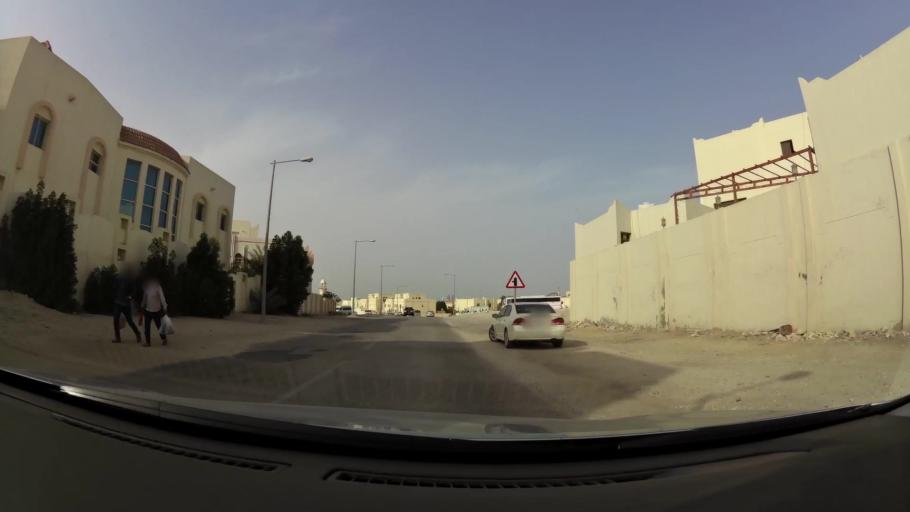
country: QA
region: Baladiyat ad Dawhah
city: Doha
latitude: 25.3176
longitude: 51.5006
